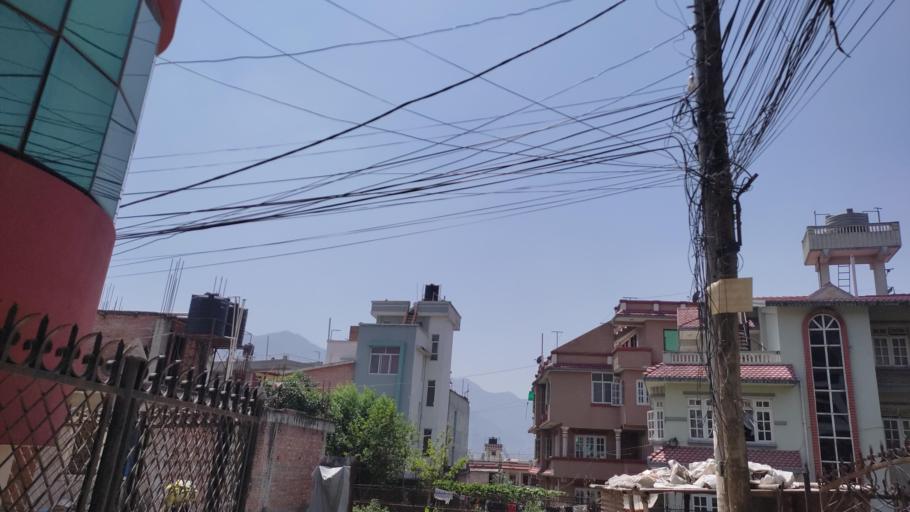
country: NP
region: Central Region
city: Kirtipur
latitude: 27.6752
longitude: 85.2724
